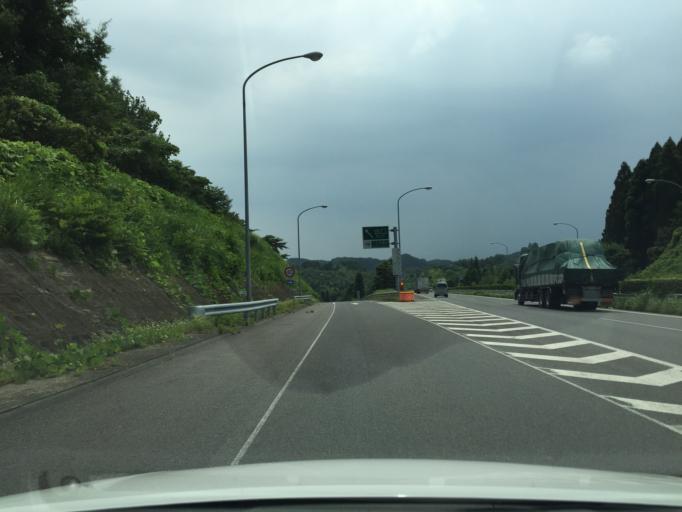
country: JP
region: Fukushima
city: Iwaki
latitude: 37.0051
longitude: 140.8117
